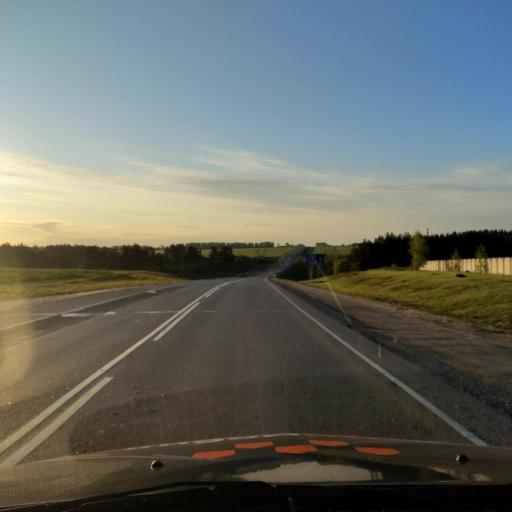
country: RU
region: Orjol
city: Livny
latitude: 52.4493
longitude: 37.5087
